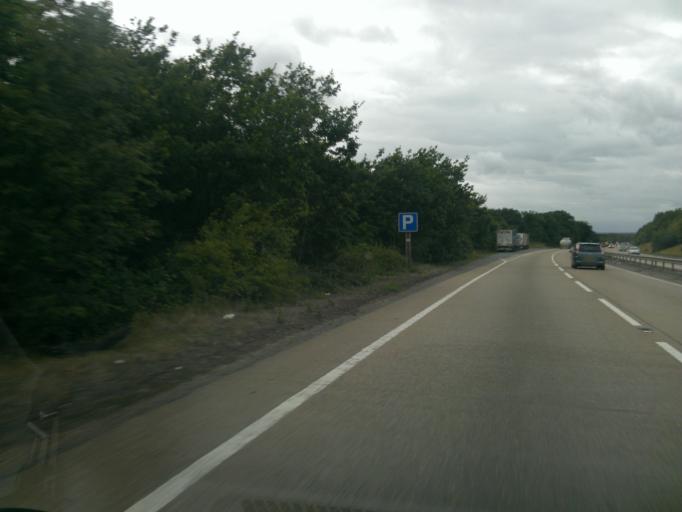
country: GB
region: England
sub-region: Essex
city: Alresford
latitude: 51.8878
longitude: 1.0180
